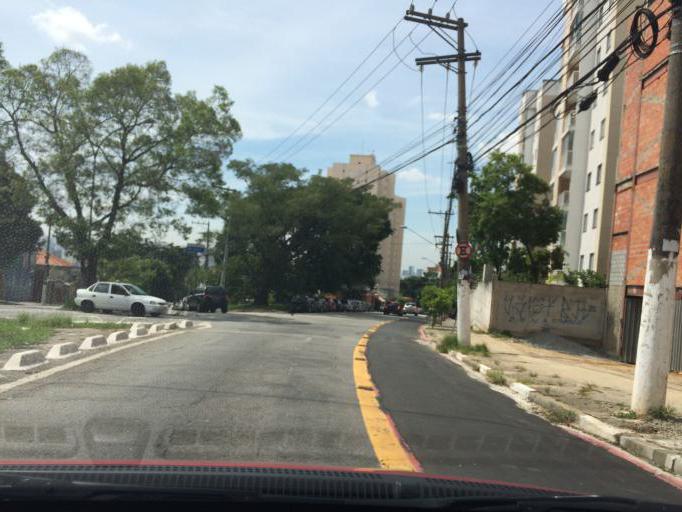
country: BR
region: Sao Paulo
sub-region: Osasco
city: Osasco
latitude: -23.5483
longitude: -46.7471
